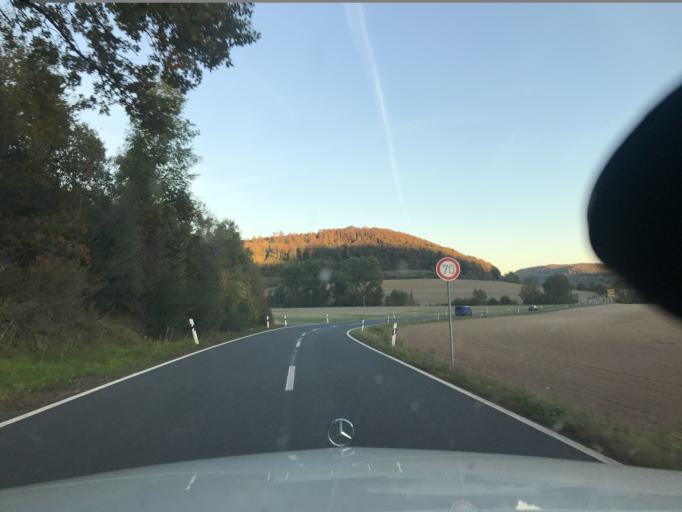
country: DE
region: Thuringia
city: Geismar
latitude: 51.2262
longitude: 10.1833
